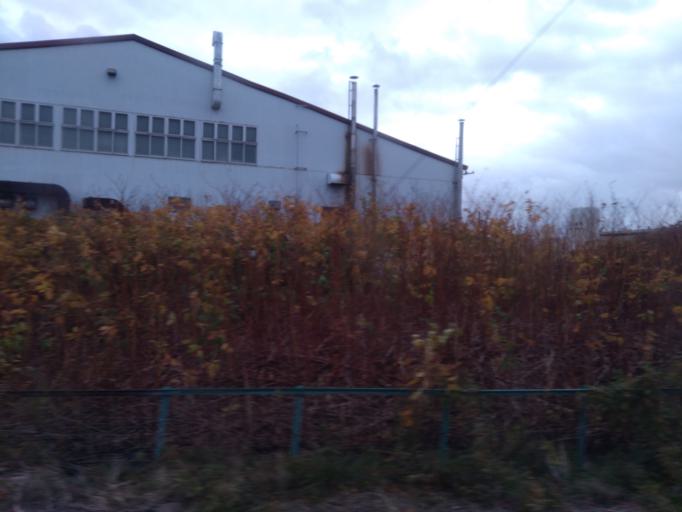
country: JP
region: Hokkaido
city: Hakodate
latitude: 41.8073
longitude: 140.7327
